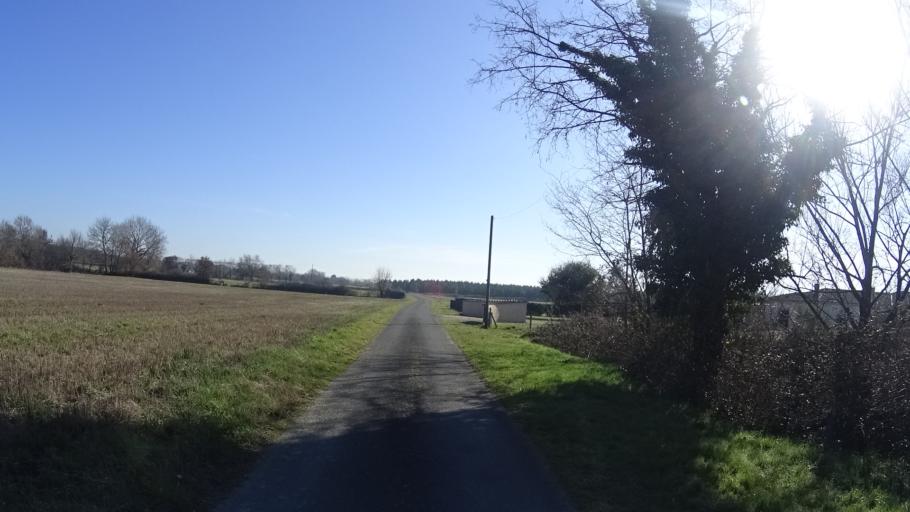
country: FR
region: Aquitaine
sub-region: Departement de la Dordogne
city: Montpon-Menesterol
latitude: 45.0336
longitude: 0.2284
